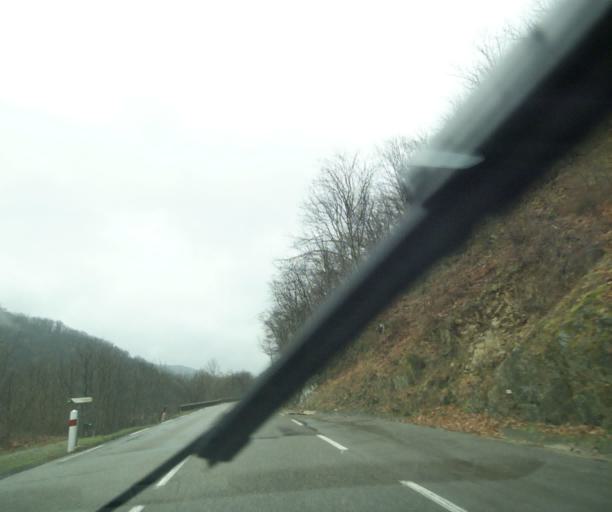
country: FR
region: Rhone-Alpes
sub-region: Departement de l'Ardeche
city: Thueyts
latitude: 44.6647
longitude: 4.1302
